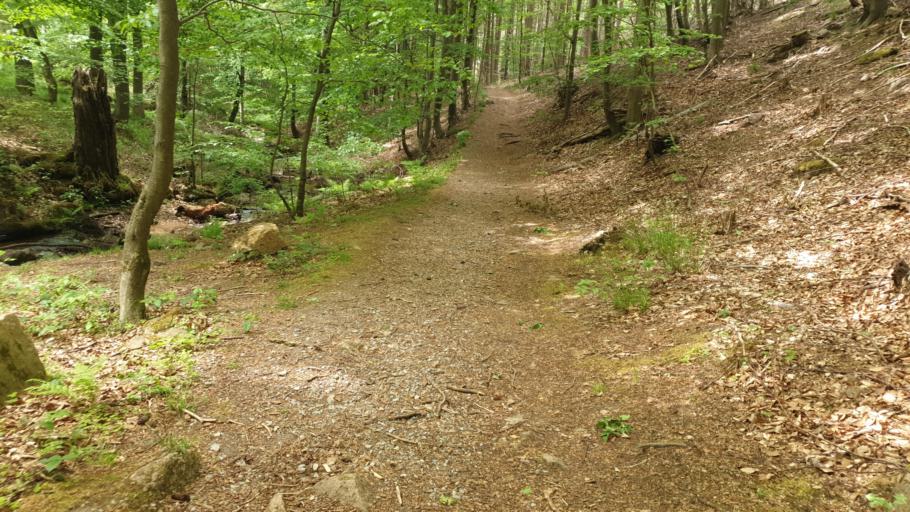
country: DE
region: Saxony-Anhalt
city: Ilsenburg
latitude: 51.8390
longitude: 10.6567
